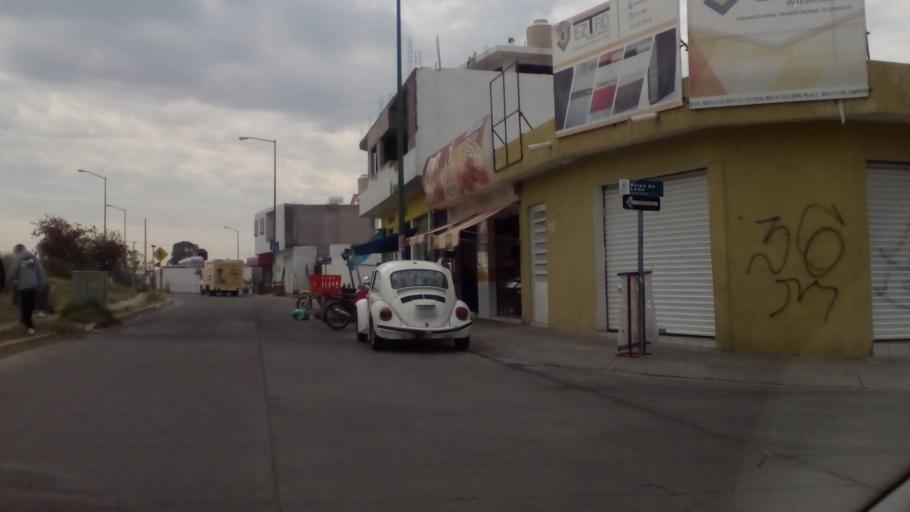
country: MX
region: Guanajuato
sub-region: Leon
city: Fraccionamiento Paseo de las Torres
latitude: 21.1878
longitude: -101.7646
